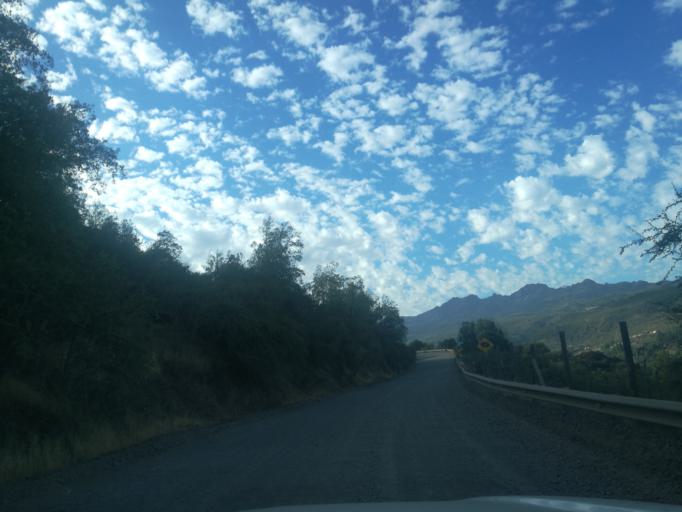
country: CL
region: O'Higgins
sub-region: Provincia de Cachapoal
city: Machali
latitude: -34.2447
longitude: -70.4694
